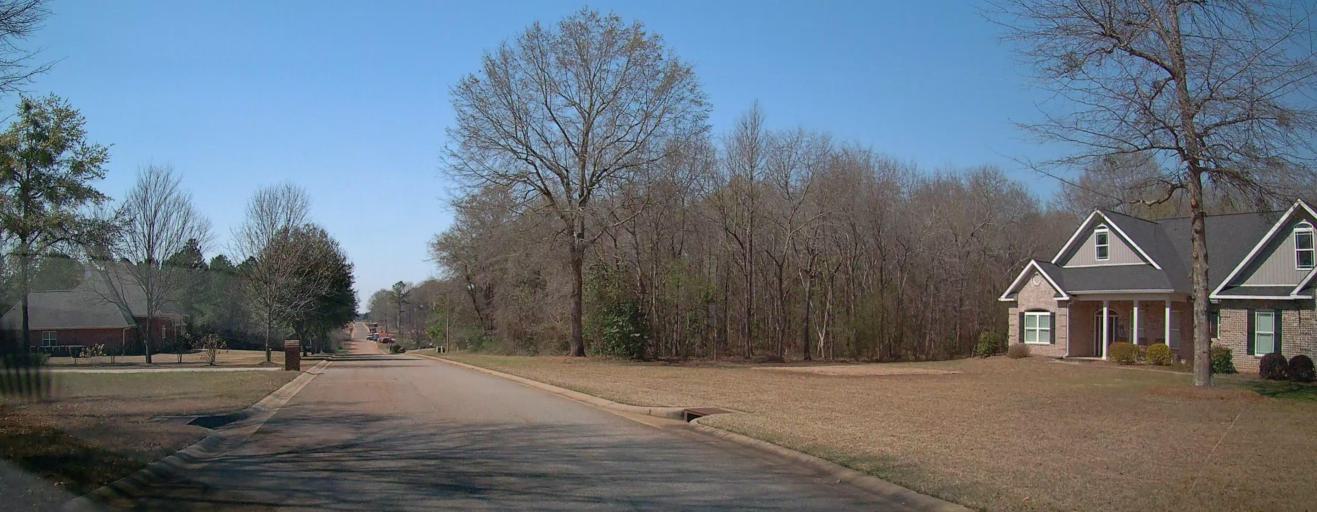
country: US
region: Georgia
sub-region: Peach County
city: Byron
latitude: 32.5970
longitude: -83.7508
